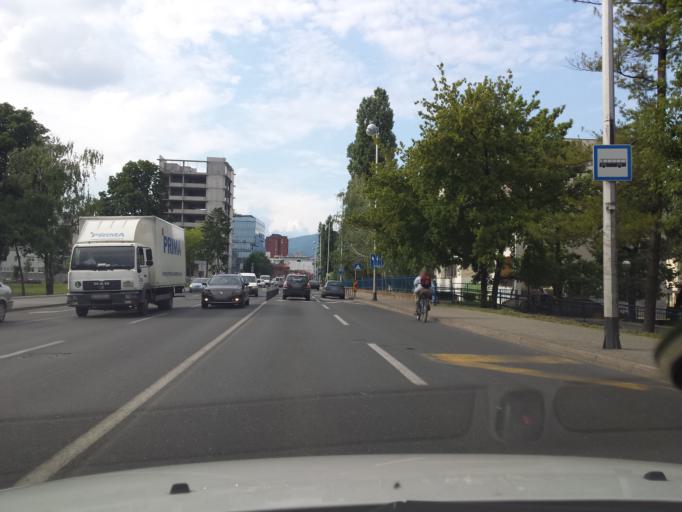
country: HR
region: Grad Zagreb
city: Zagreb - Centar
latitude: 45.8018
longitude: 15.9434
